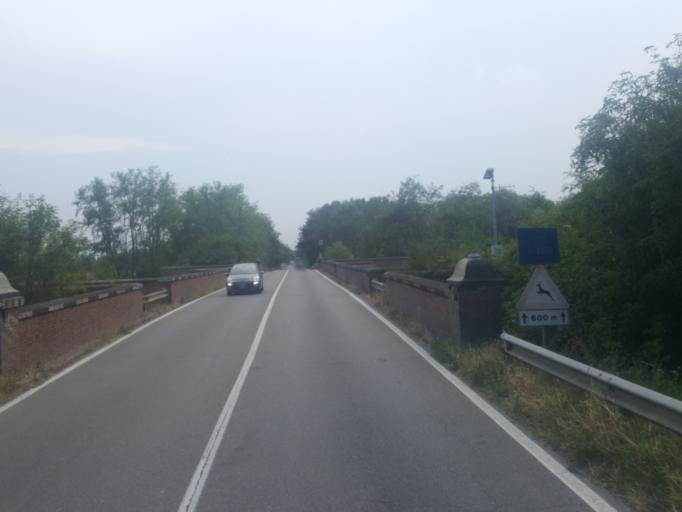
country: IT
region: Emilia-Romagna
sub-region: Provincia di Modena
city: Gaggio
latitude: 44.6232
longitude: 10.9978
